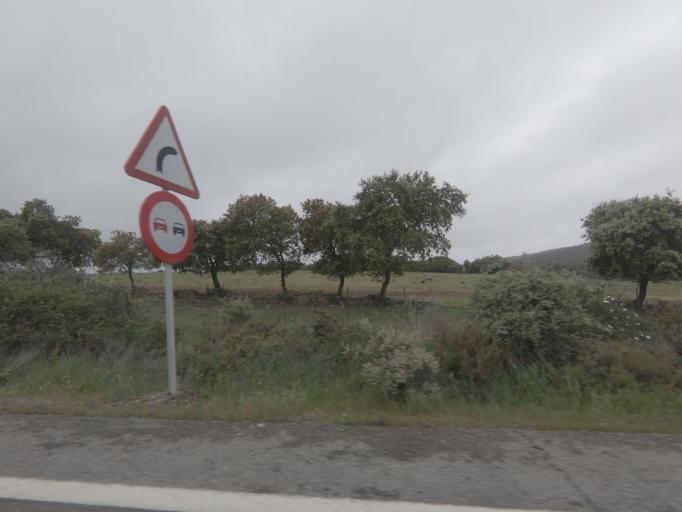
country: ES
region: Extremadura
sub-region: Provincia de Caceres
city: Malpartida de Caceres
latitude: 39.2964
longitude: -6.5190
